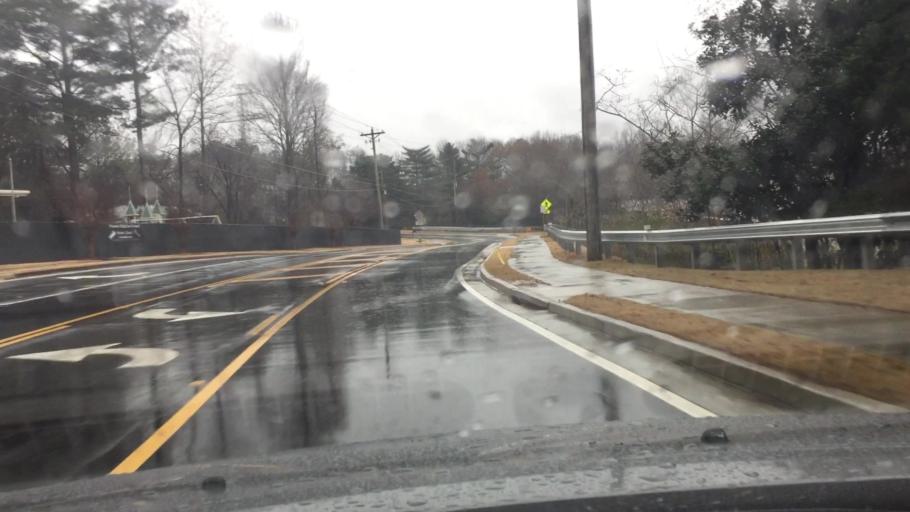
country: US
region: Georgia
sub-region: Cobb County
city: Kennesaw
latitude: 33.9904
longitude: -84.6076
